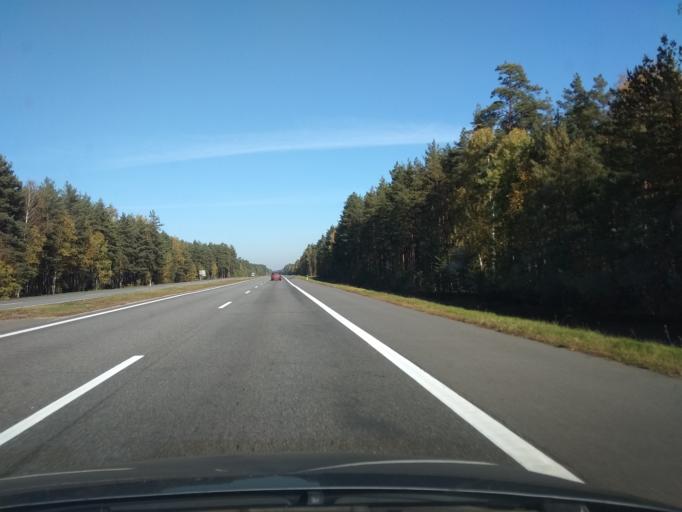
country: BY
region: Brest
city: Baranovichi
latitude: 52.9487
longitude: 25.7152
